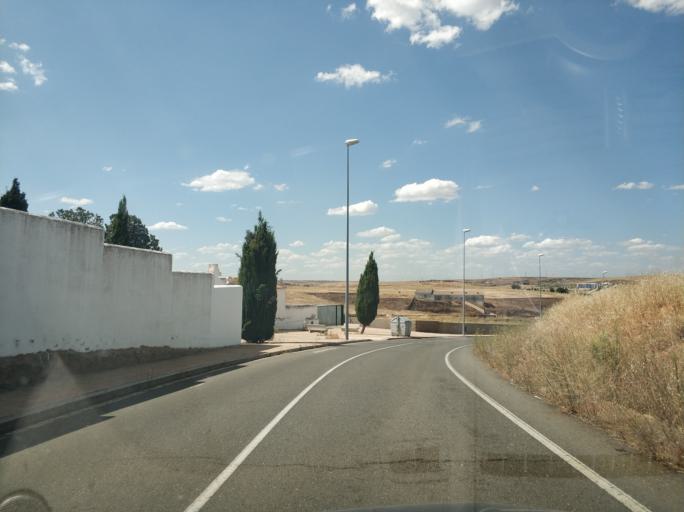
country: ES
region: Castille and Leon
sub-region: Provincia de Salamanca
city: Aldeatejada
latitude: 40.9483
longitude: -5.6944
